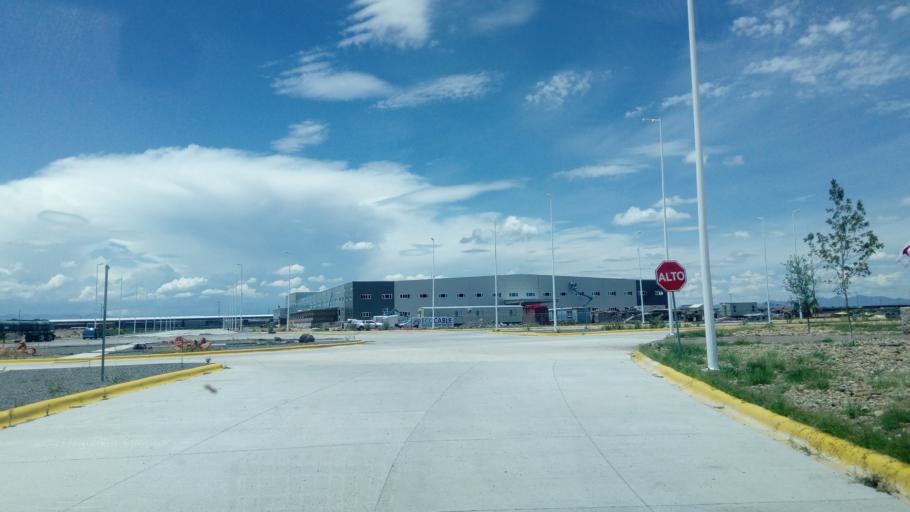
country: MX
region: Durango
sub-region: Durango
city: Jose Refugio Salcido
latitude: 24.1603
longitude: -104.5149
